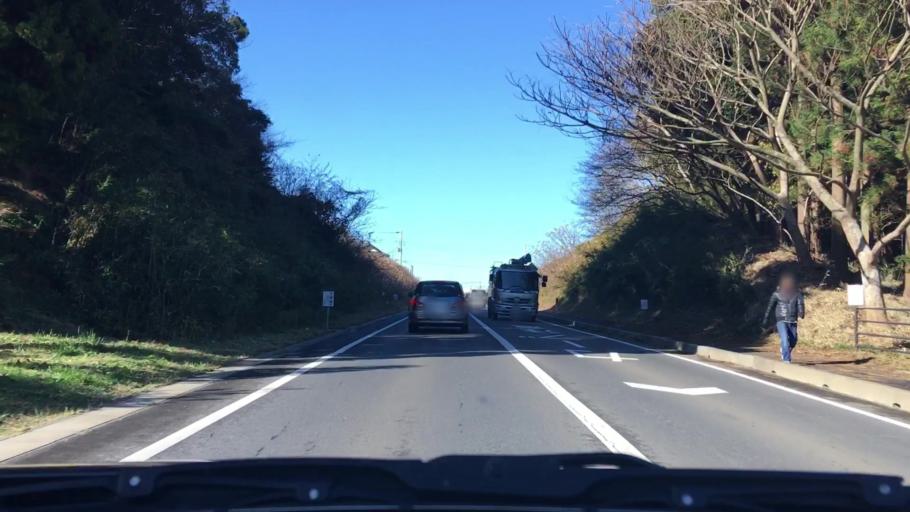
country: JP
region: Chiba
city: Omigawa
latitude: 35.8387
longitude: 140.5593
